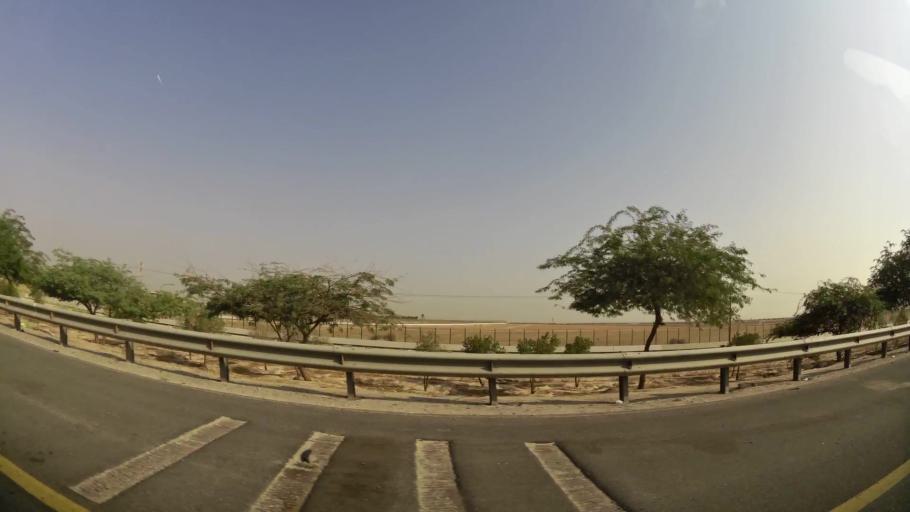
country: KW
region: Mubarak al Kabir
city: Mubarak al Kabir
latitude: 29.1823
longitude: 48.0232
